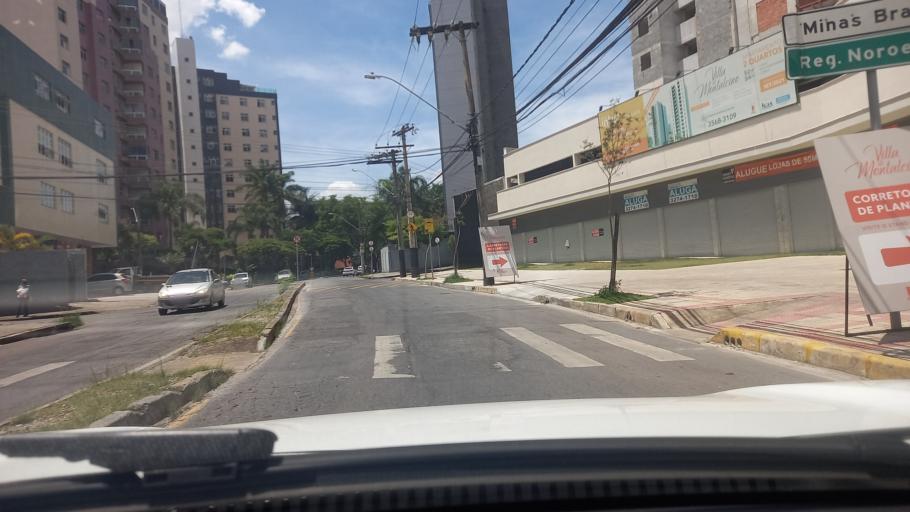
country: BR
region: Minas Gerais
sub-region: Belo Horizonte
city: Belo Horizonte
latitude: -19.9189
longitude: -43.9872
